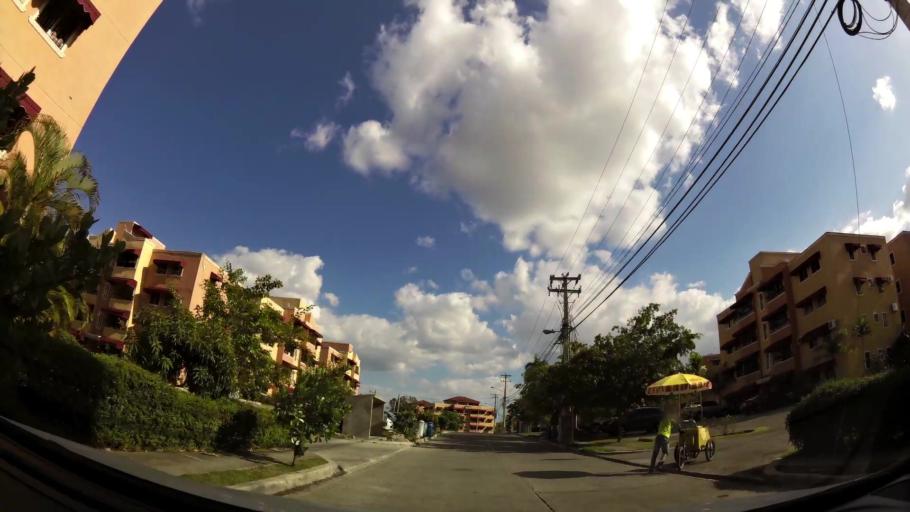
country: DO
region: Nacional
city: Santo Domingo
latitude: 18.5129
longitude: -69.9836
